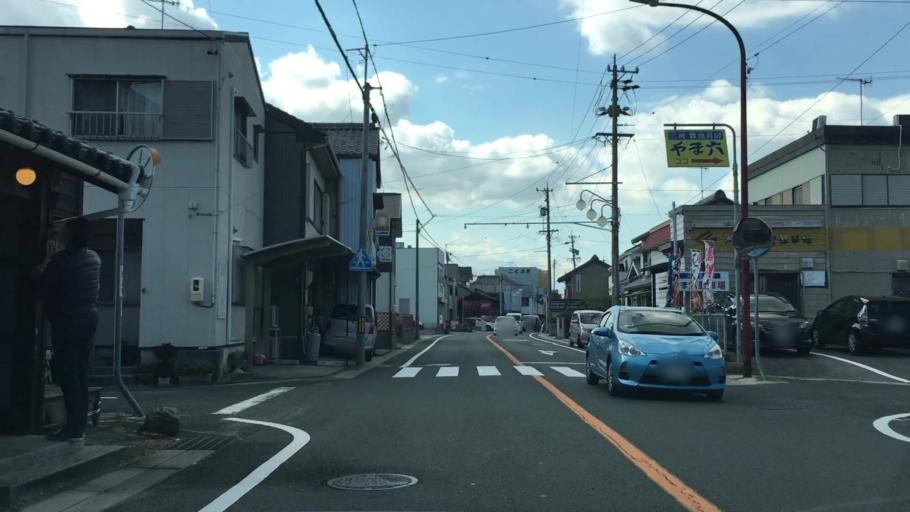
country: JP
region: Aichi
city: Gamagori
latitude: 34.8169
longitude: 137.2419
